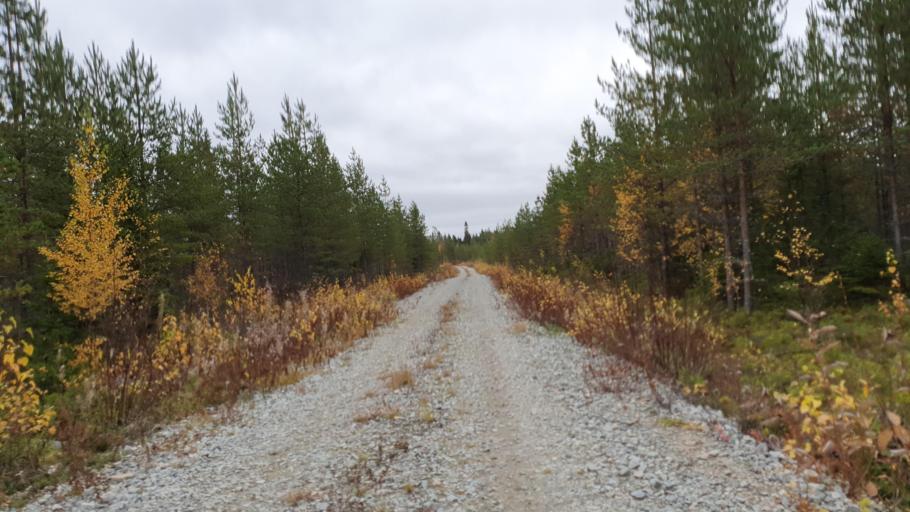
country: FI
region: Kainuu
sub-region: Kehys-Kainuu
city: Kuhmo
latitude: 64.4477
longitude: 29.6043
